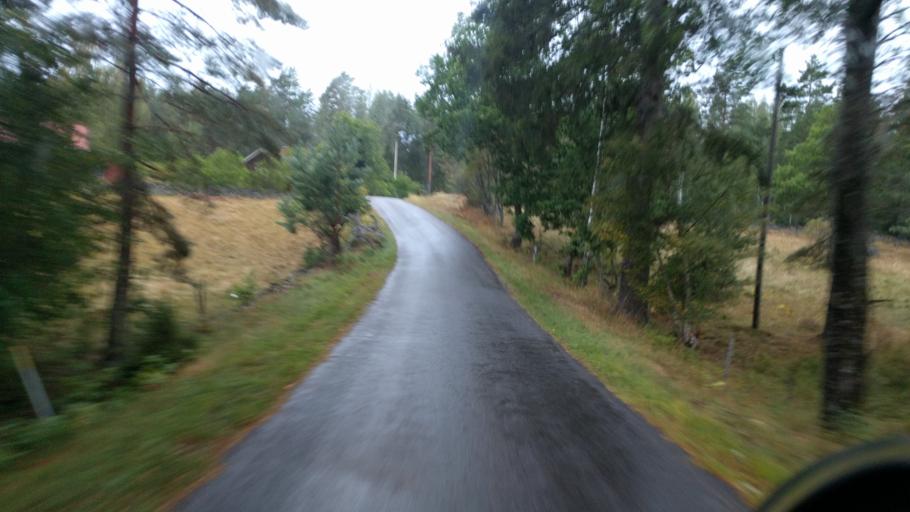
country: SE
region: Kalmar
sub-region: Vasterviks Kommun
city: Ankarsrum
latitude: 57.8259
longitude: 16.2764
